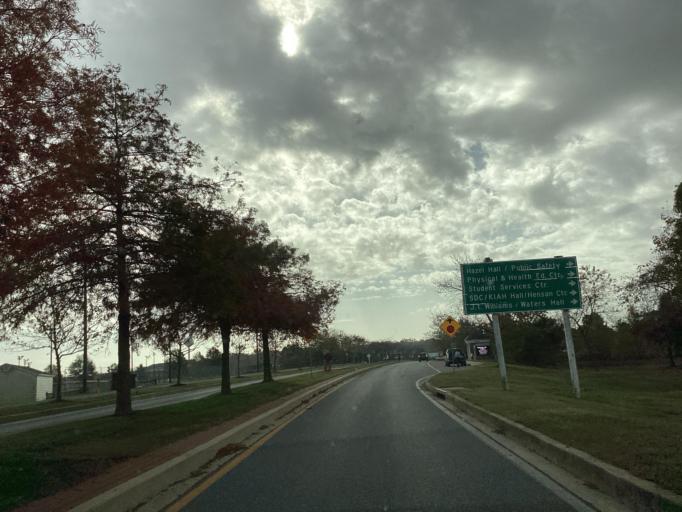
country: US
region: Maryland
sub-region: Somerset County
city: Princess Anne
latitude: 38.2149
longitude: -75.6872
